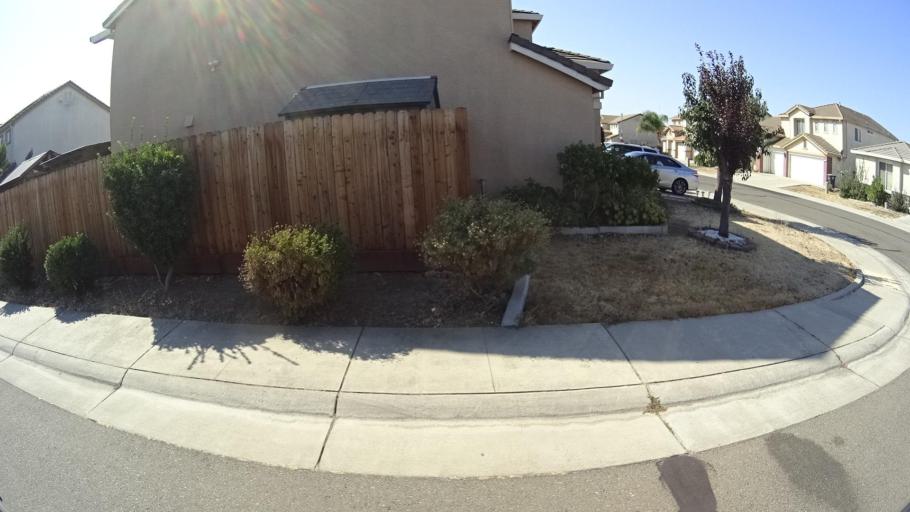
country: US
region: California
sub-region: Sacramento County
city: Laguna
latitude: 38.4449
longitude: -121.3944
